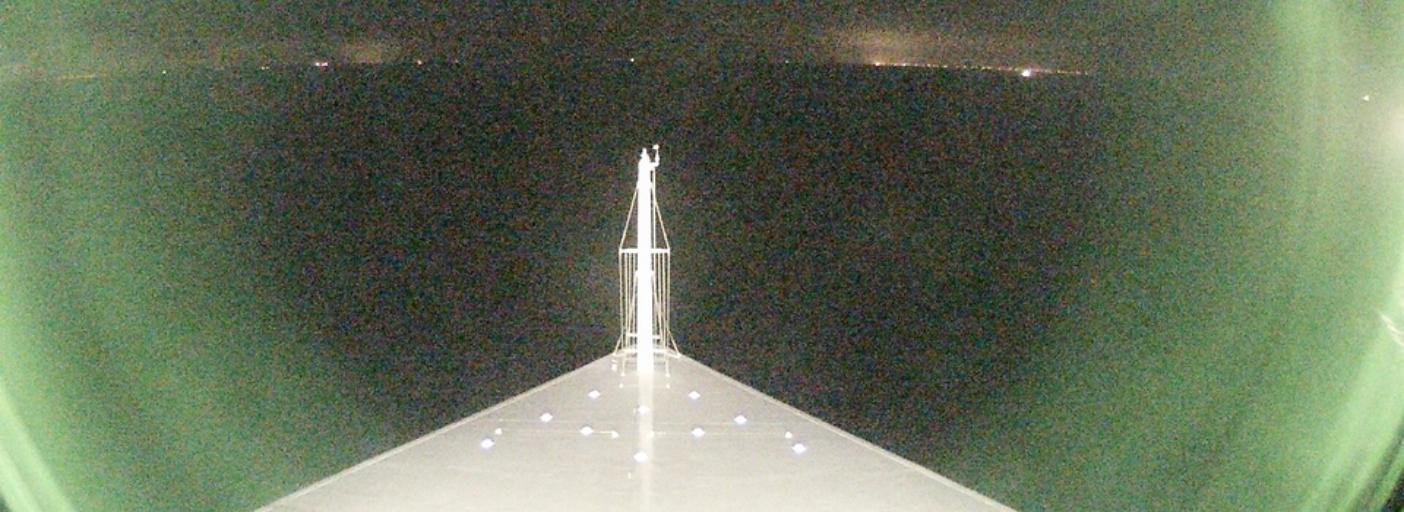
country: DE
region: Lower Saxony
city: Spiekeroog
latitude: 54.0033
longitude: 7.5890
